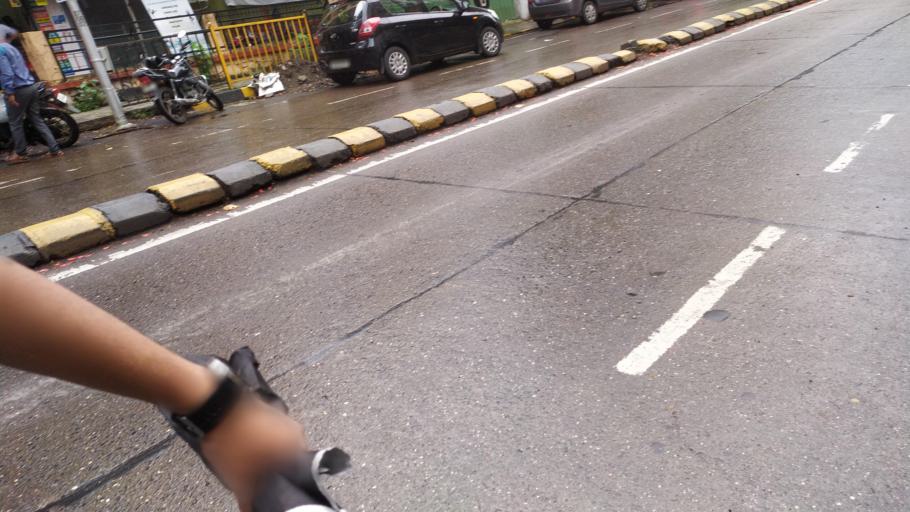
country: IN
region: Maharashtra
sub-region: Mumbai Suburban
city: Borivli
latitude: 19.2422
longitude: 72.8544
